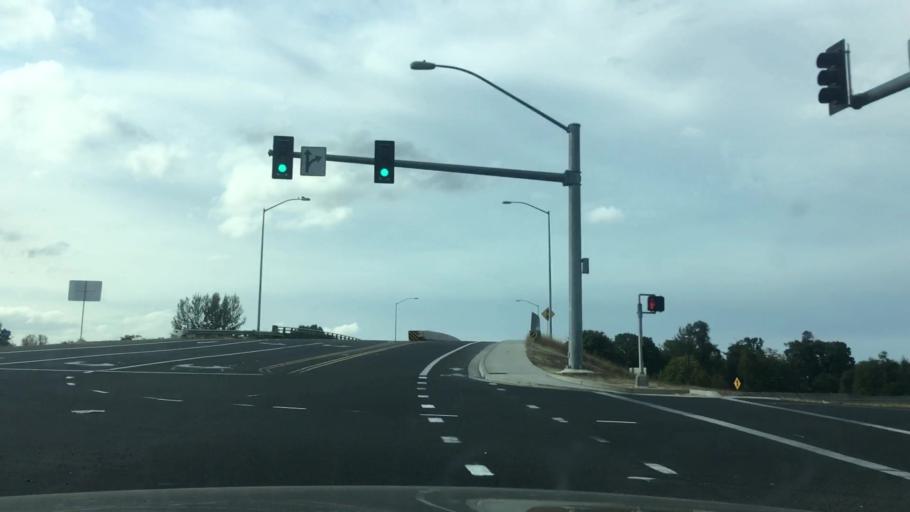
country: US
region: Oregon
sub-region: Lane County
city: Eugene
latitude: 44.0844
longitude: -123.1011
